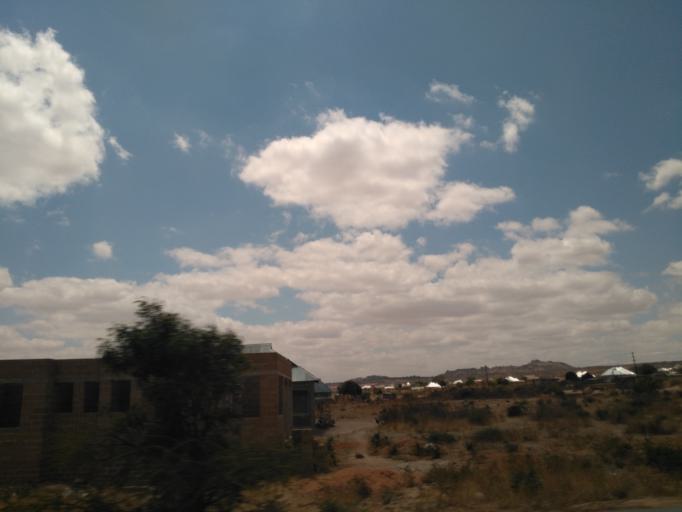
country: TZ
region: Dodoma
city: Kisasa
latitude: -6.1824
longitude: 35.7934
